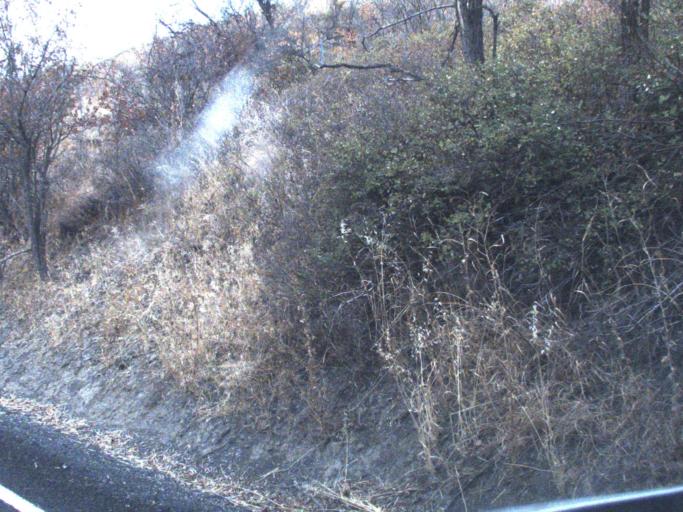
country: US
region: Washington
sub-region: Okanogan County
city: Coulee Dam
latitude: 47.8491
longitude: -118.7175
